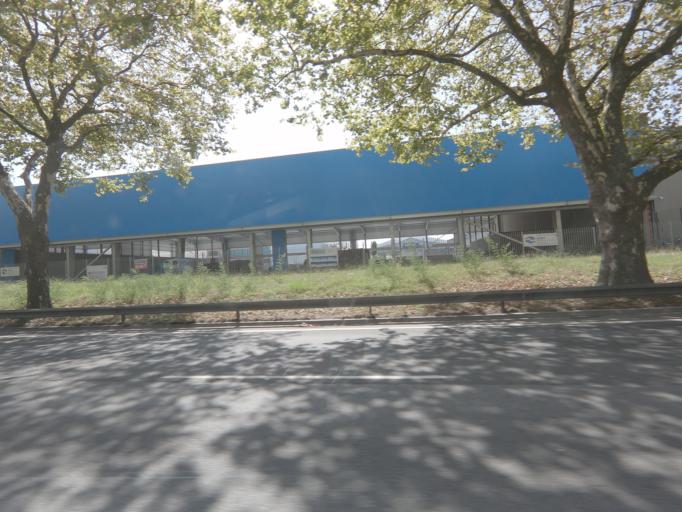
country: PT
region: Porto
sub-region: Matosinhos
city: Senhora da Hora
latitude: 41.1740
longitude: -8.6506
